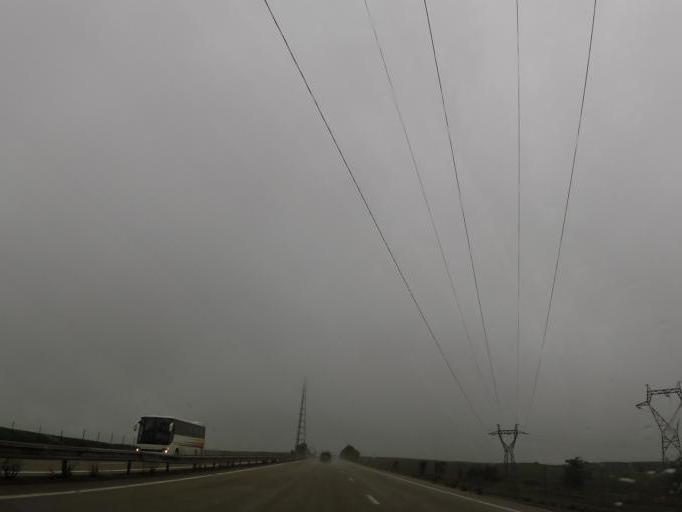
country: FR
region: Champagne-Ardenne
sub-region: Departement de la Marne
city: Gueux
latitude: 49.2392
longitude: 3.8762
